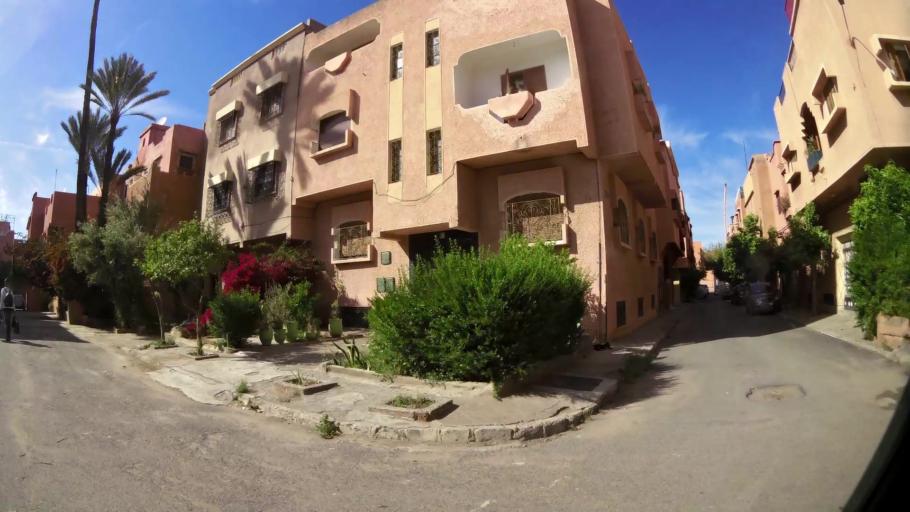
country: MA
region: Marrakech-Tensift-Al Haouz
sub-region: Marrakech
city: Marrakesh
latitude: 31.6549
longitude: -8.0168
